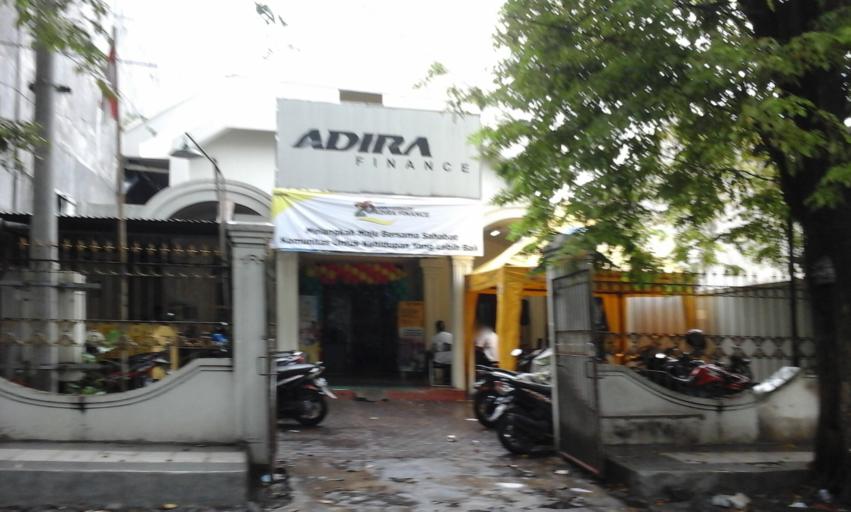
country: ID
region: East Java
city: Kadipaten
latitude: -8.1302
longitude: 113.2166
